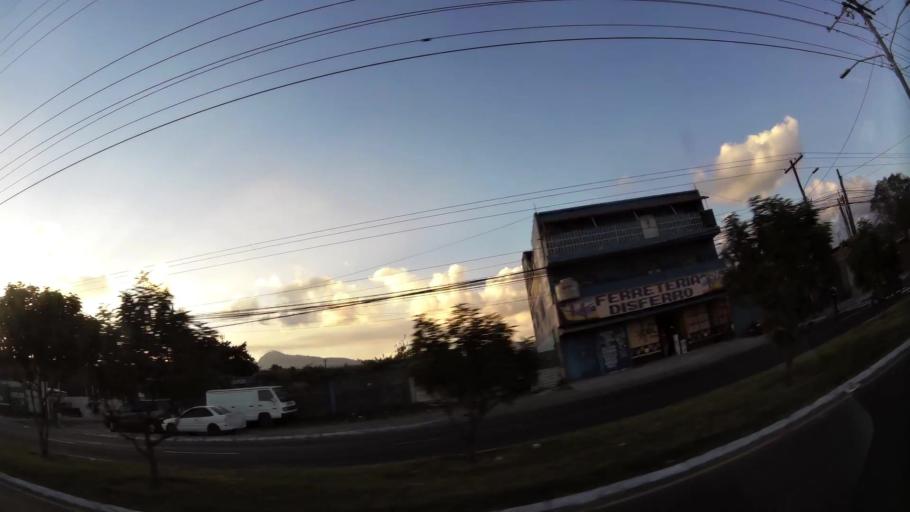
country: GT
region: Guatemala
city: Villa Nueva
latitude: 14.5111
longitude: -90.5800
